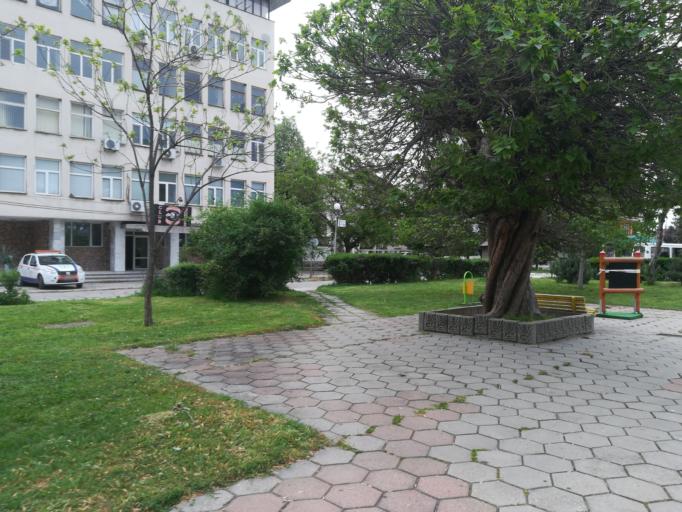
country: BG
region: Stara Zagora
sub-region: Obshtina Chirpan
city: Chirpan
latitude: 42.0990
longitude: 25.2279
